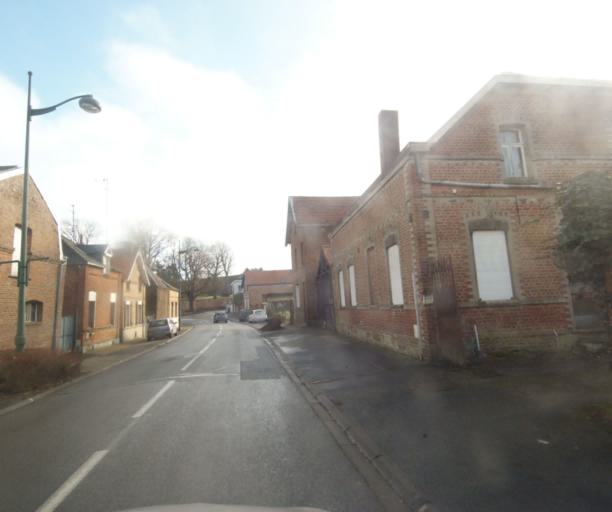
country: FR
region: Nord-Pas-de-Calais
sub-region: Departement du Nord
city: Artres
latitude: 50.2915
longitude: 3.5379
